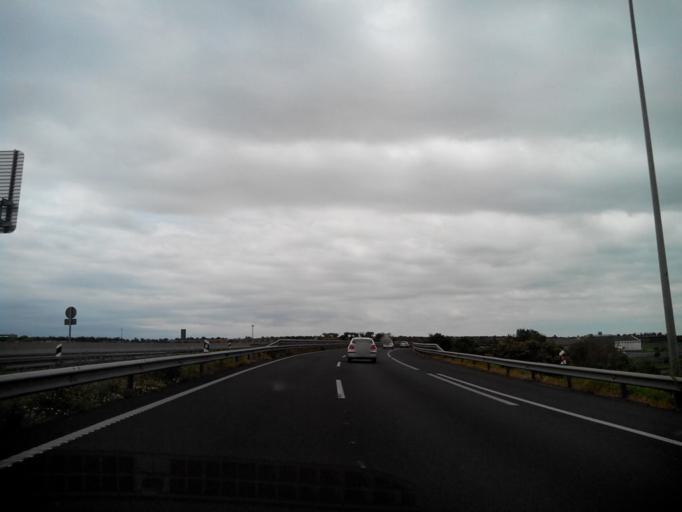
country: ES
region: Catalonia
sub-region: Provincia de Lleida
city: Anglesola
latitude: 41.6512
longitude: 1.0958
